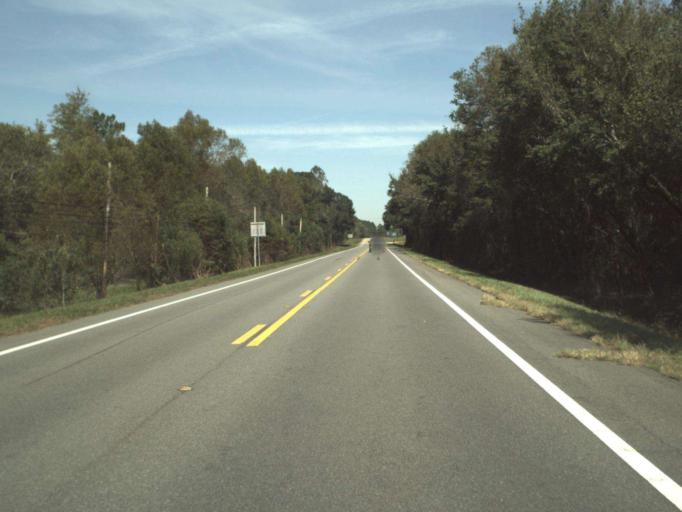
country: US
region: Florida
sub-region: Washington County
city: Chipley
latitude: 30.8269
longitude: -85.5330
